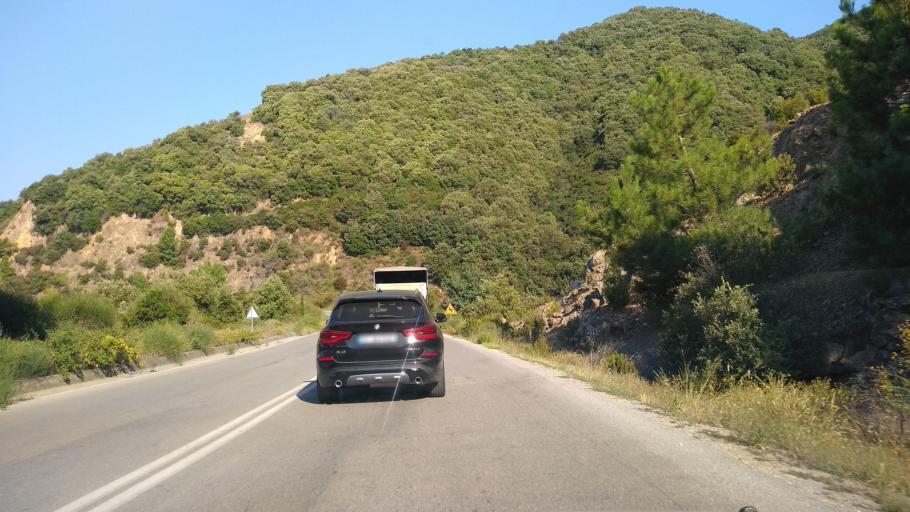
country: GR
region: Central Macedonia
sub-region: Nomos Chalkidikis
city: Stratonion
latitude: 40.5200
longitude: 23.8122
